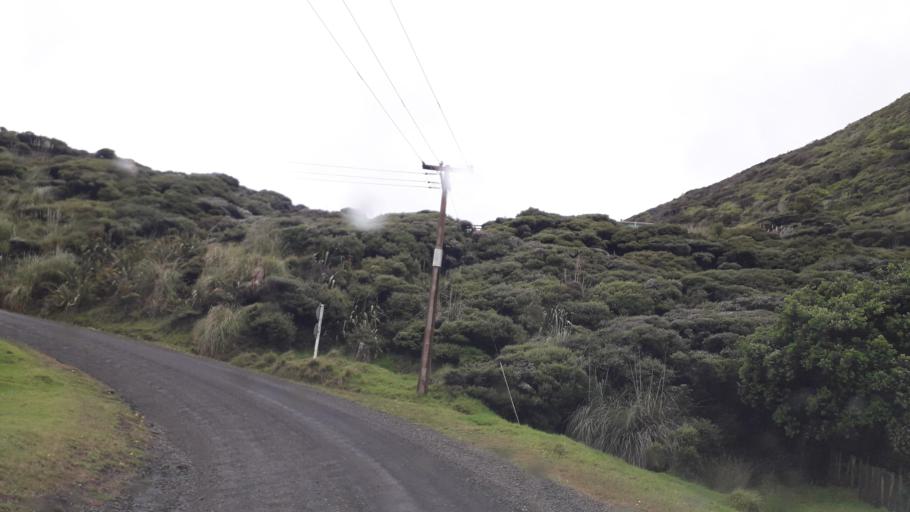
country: NZ
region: Northland
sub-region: Far North District
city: Ahipara
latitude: -35.4333
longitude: 173.2820
